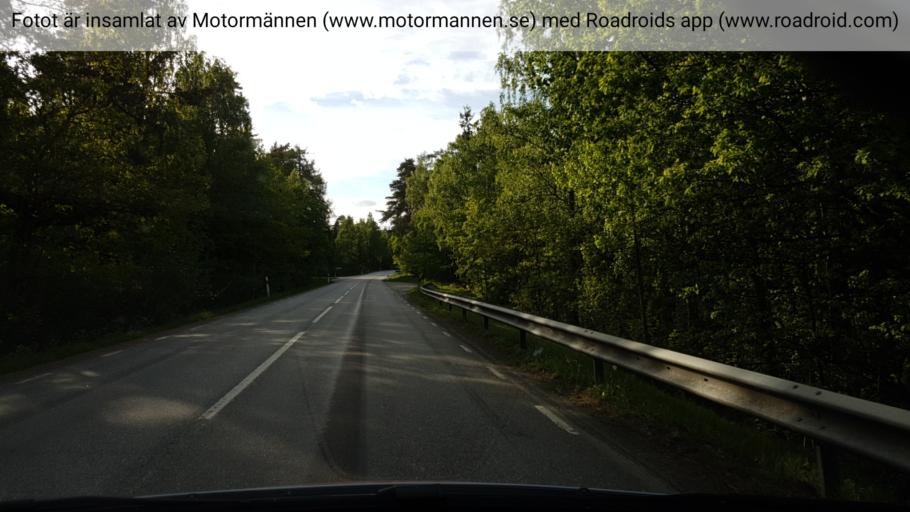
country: SE
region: Vaestmanland
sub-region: Hallstahammars Kommun
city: Hallstahammar
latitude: 59.6553
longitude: 16.1859
